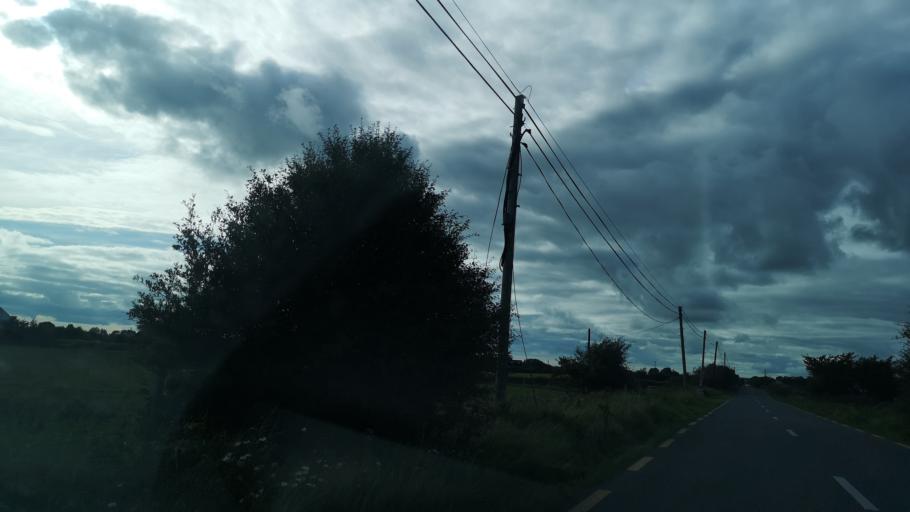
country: IE
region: Connaught
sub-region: County Galway
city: Ballinasloe
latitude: 53.2887
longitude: -8.0859
